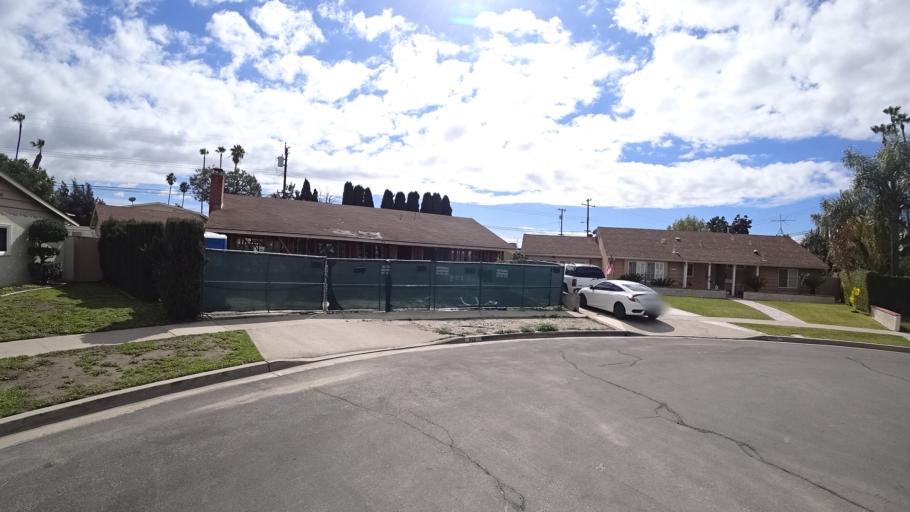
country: US
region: California
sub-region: Orange County
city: Anaheim
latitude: 33.8200
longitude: -117.9475
